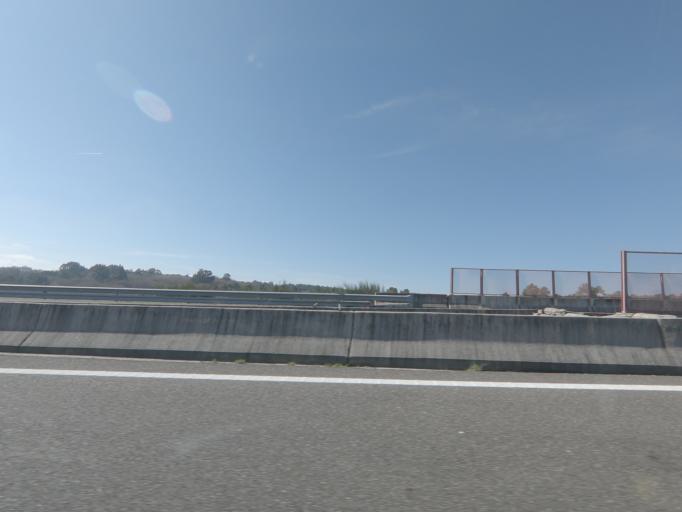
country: ES
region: Galicia
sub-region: Provincia de Ourense
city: Maside
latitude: 42.4197
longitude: -8.0169
